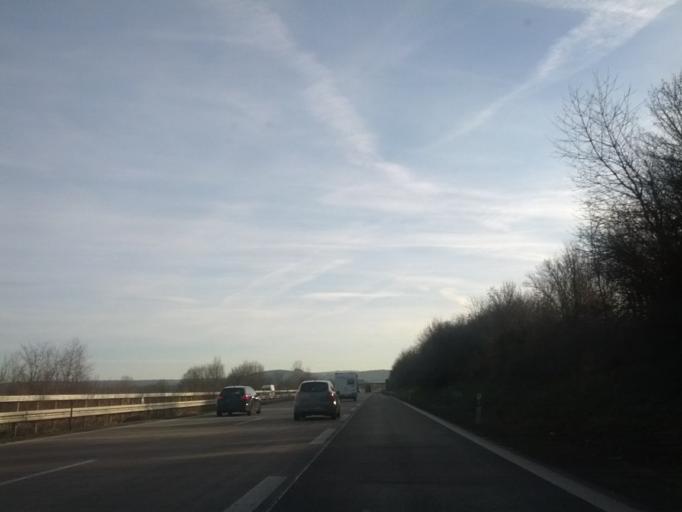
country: DE
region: Baden-Wuerttemberg
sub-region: Regierungsbezirk Stuttgart
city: Ellwangen
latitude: 48.9524
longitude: 10.1875
